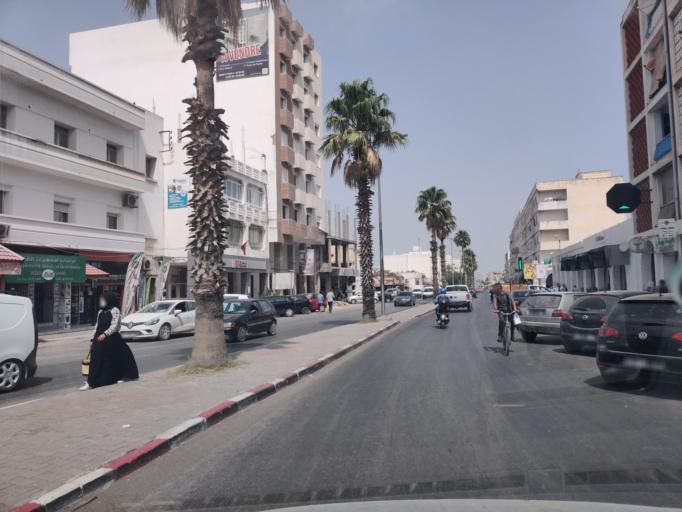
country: TN
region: Nabul
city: Bu `Urqub
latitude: 36.5986
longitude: 10.4989
